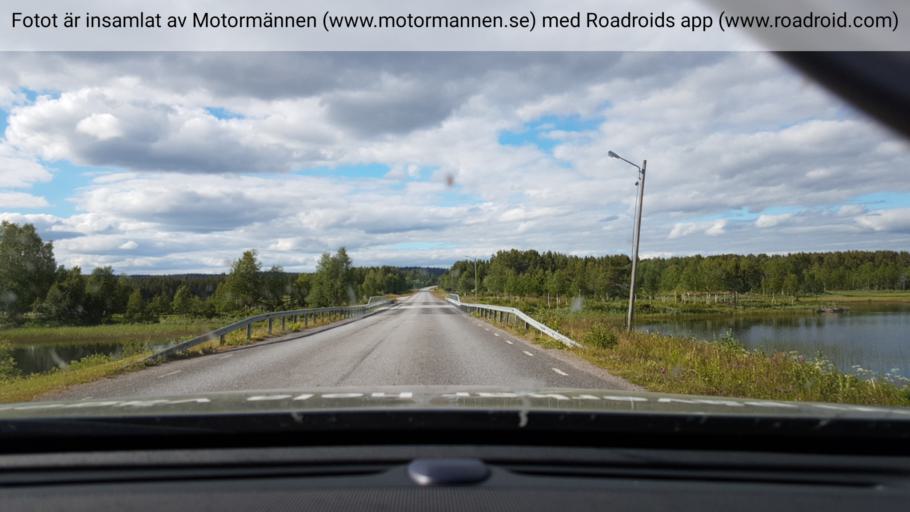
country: SE
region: Norrbotten
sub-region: Arjeplogs Kommun
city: Arjeplog
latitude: 66.2522
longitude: 17.2038
